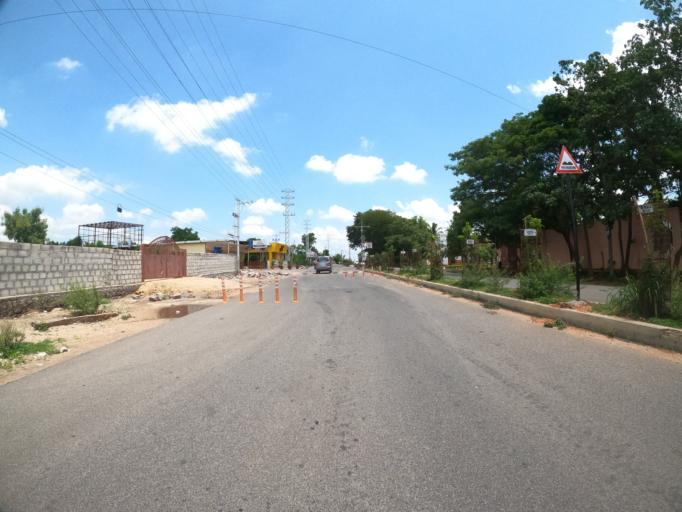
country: IN
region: Telangana
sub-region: Rangareddi
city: Singapur
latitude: 17.4186
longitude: 78.2192
